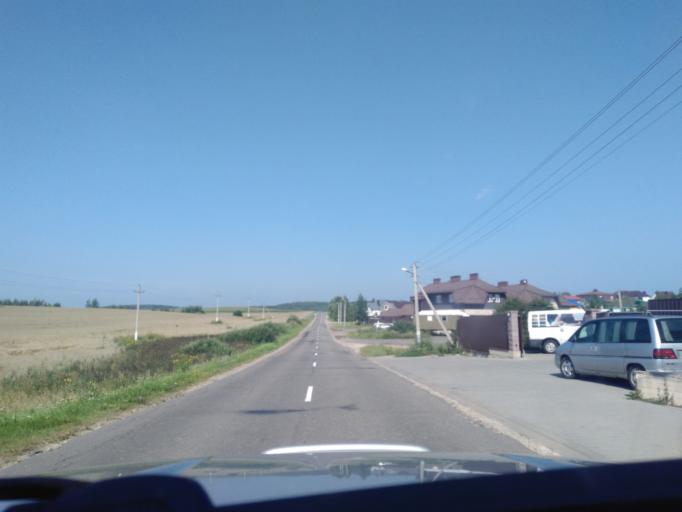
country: BY
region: Minsk
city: Zhdanovichy
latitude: 53.9339
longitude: 27.4057
